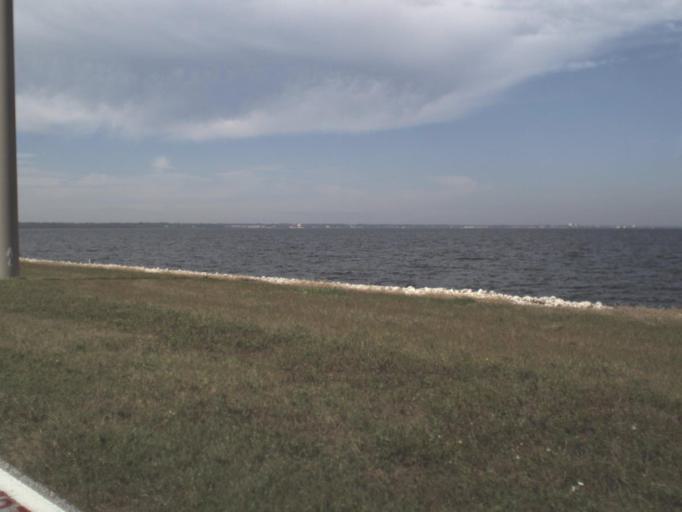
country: US
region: Florida
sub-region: Brevard County
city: Port Saint John
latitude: 28.5271
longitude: -80.7511
